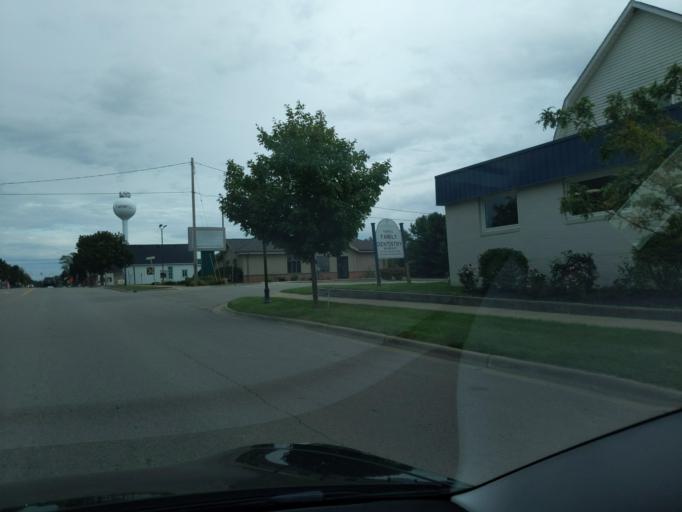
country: US
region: Michigan
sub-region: Clare County
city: Clare
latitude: 43.8353
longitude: -84.8701
